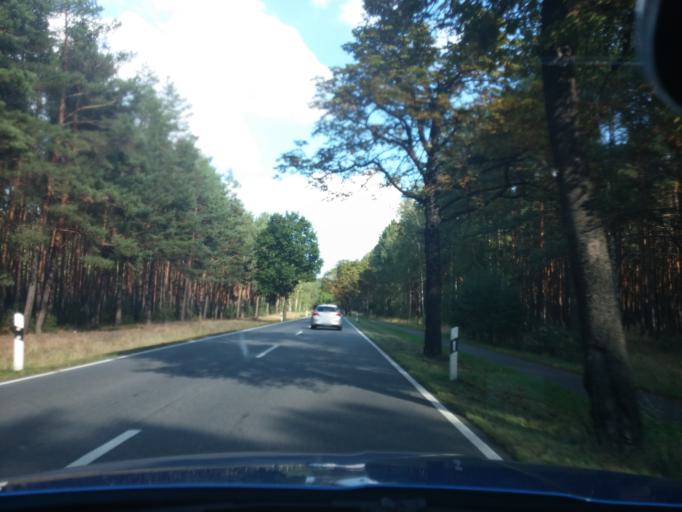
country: DE
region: Brandenburg
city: Halbe
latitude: 52.1066
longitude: 13.7157
